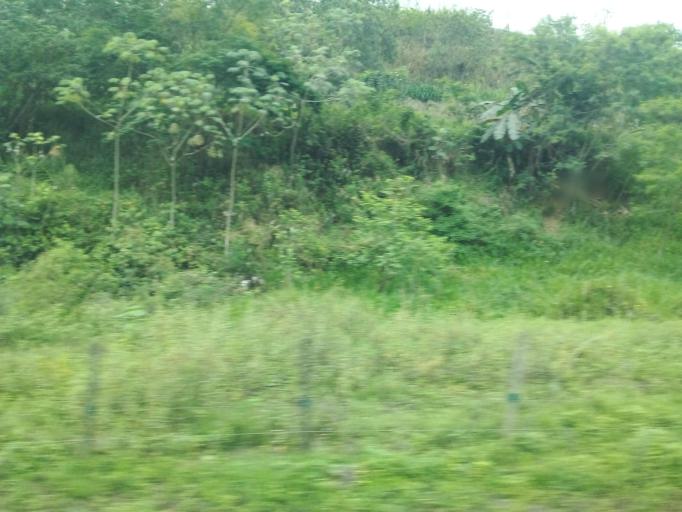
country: BR
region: Minas Gerais
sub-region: Coronel Fabriciano
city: Coronel Fabriciano
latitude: -19.5329
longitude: -42.6720
